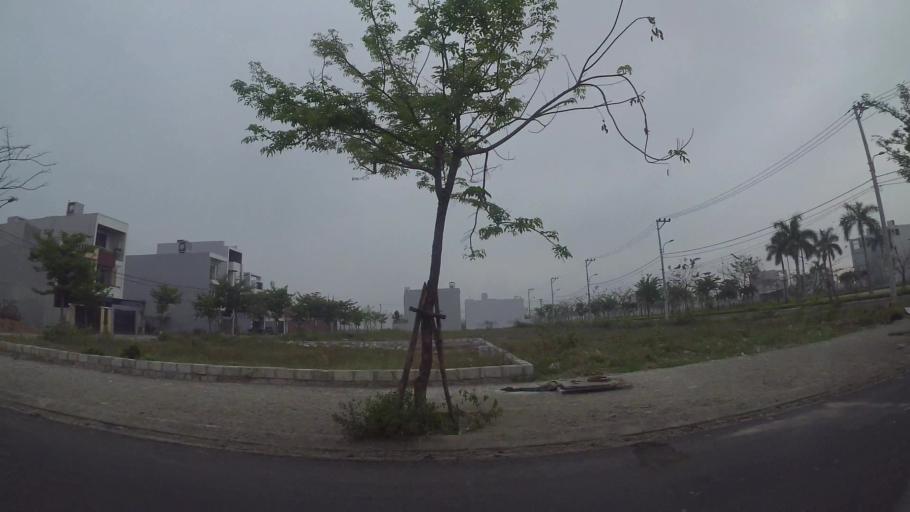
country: VN
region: Da Nang
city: Ngu Hanh Son
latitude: 16.0201
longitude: 108.2336
